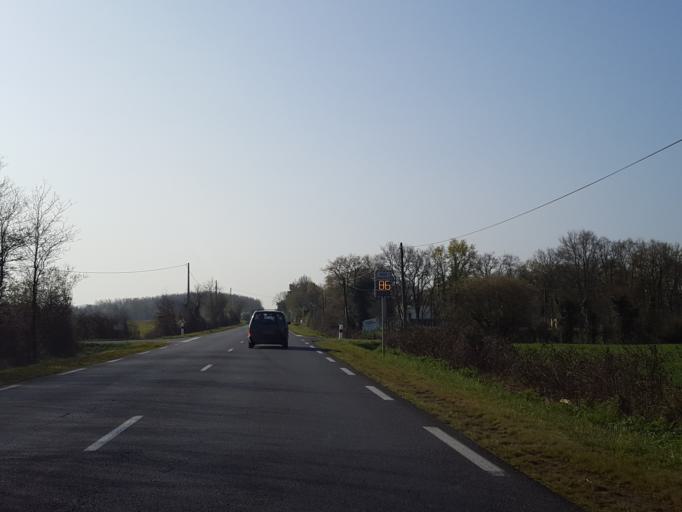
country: FR
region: Pays de la Loire
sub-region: Departement de la Loire-Atlantique
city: Geneston
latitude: 47.0792
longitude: -1.5244
